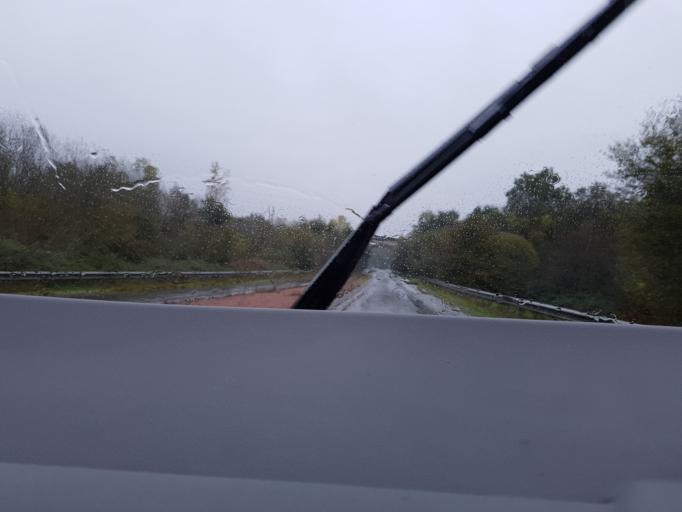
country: FR
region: Aquitaine
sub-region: Departement de la Gironde
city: Saint-Vincent-de-Paul
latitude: 44.9595
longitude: -0.4814
